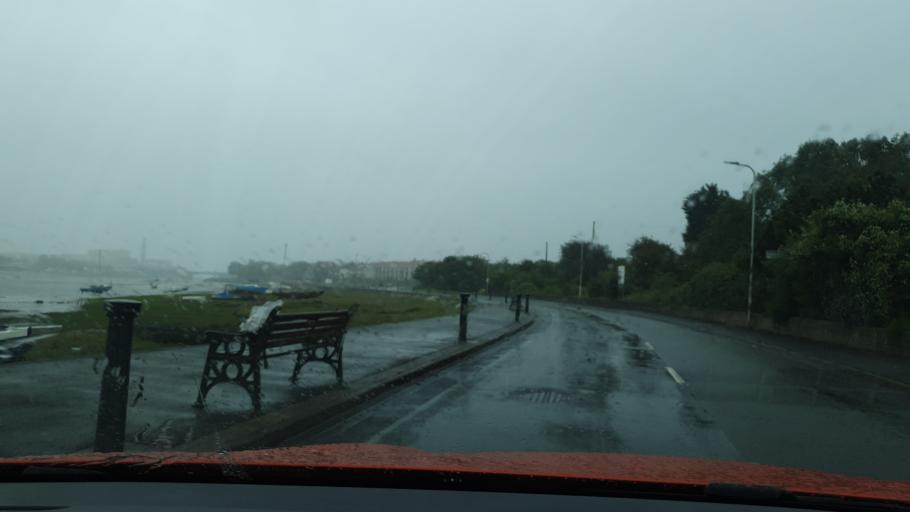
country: GB
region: England
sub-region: Cumbria
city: Barrow in Furness
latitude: 54.1164
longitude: -3.2512
